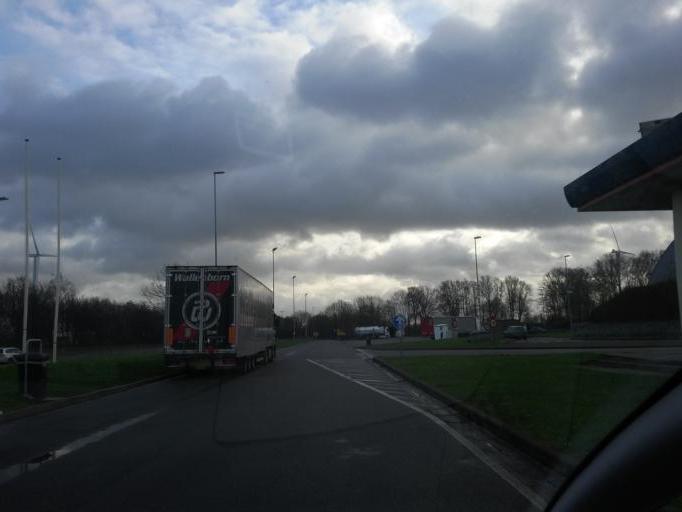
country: BE
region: Wallonia
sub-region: Province du Brabant Wallon
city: Perwez
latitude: 50.6001
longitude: 4.7901
